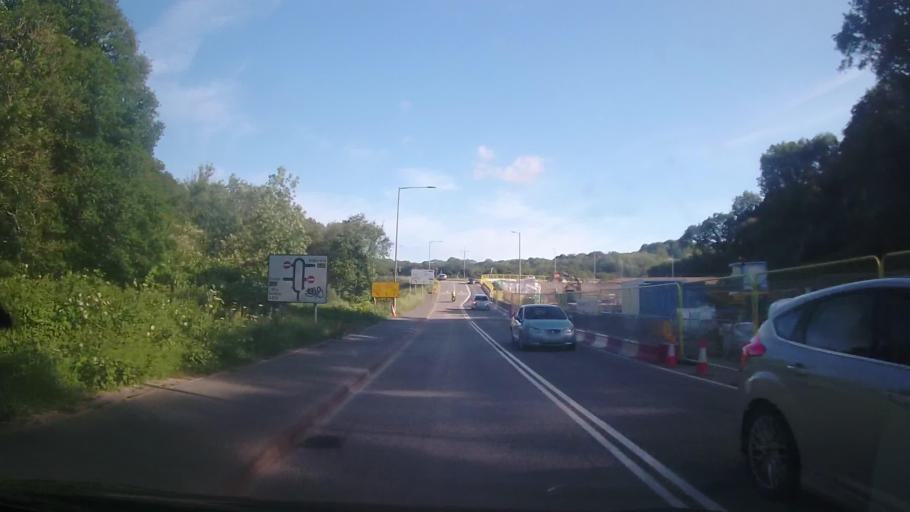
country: GB
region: England
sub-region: Devon
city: Plympton
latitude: 50.3982
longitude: -4.0982
